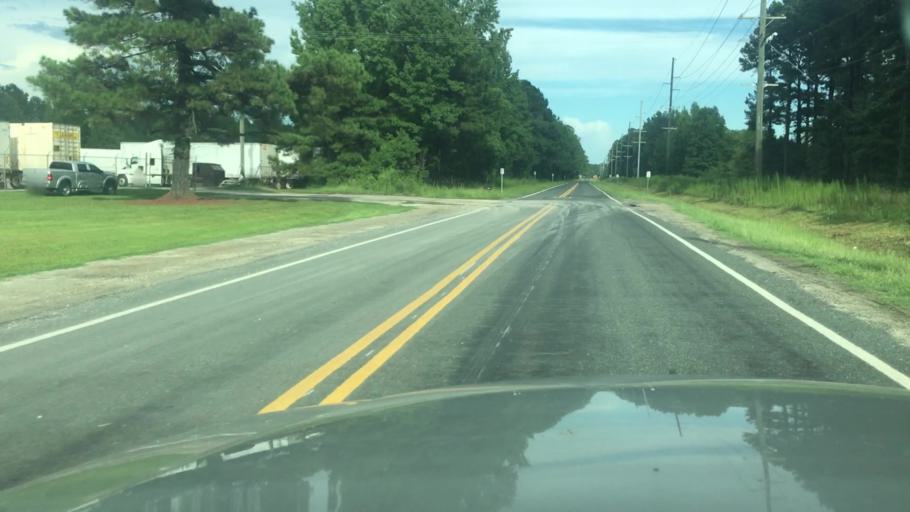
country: US
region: North Carolina
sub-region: Cumberland County
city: Eastover
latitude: 35.1648
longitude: -78.8562
